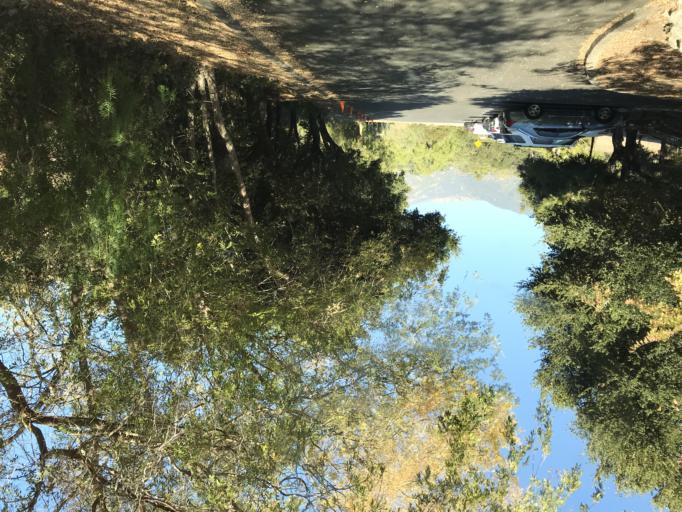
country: US
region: California
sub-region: Santa Barbara County
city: Goleta
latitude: 34.4492
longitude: -119.7772
